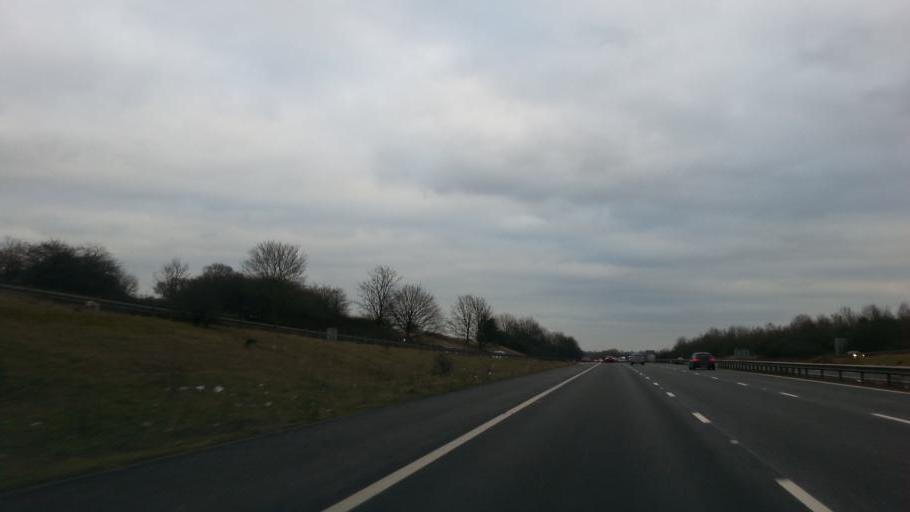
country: GB
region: England
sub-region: Warwickshire
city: Rugby
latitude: 52.4080
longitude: -1.2436
